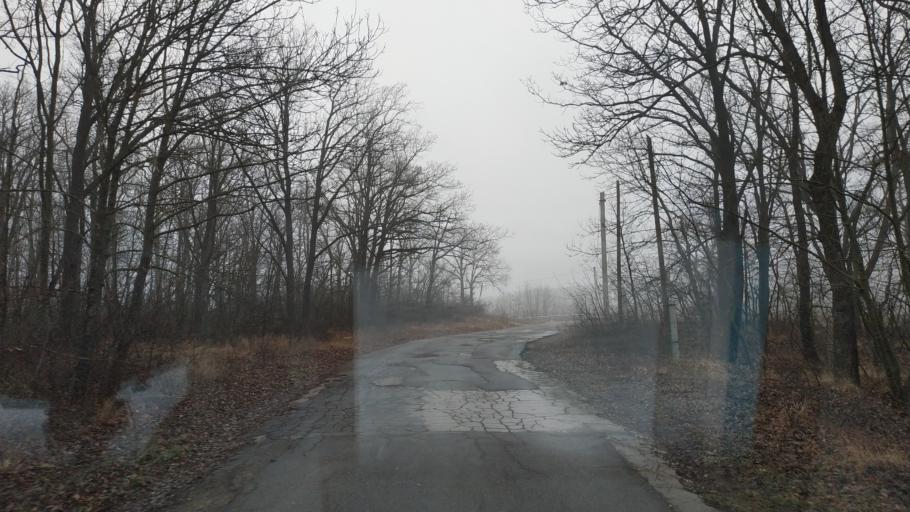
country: MD
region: Laloveni
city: Ialoveni
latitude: 46.9446
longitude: 28.7080
